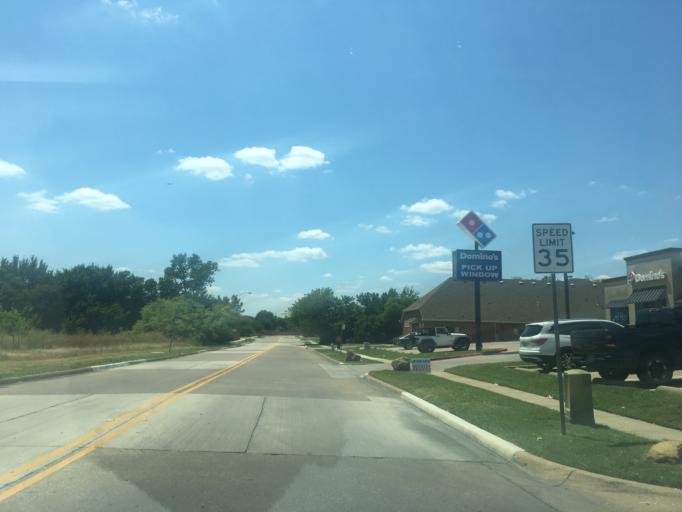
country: US
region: Texas
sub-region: Denton County
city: Lewisville
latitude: 33.0195
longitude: -96.9944
